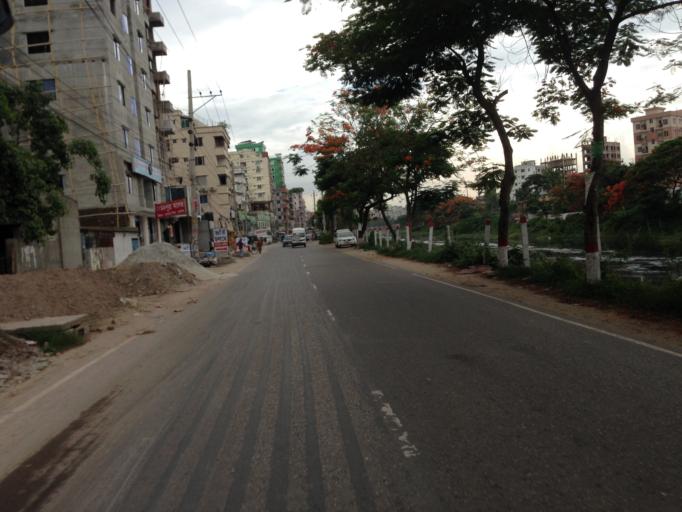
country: BD
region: Dhaka
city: Paltan
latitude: 23.7625
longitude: 90.4378
